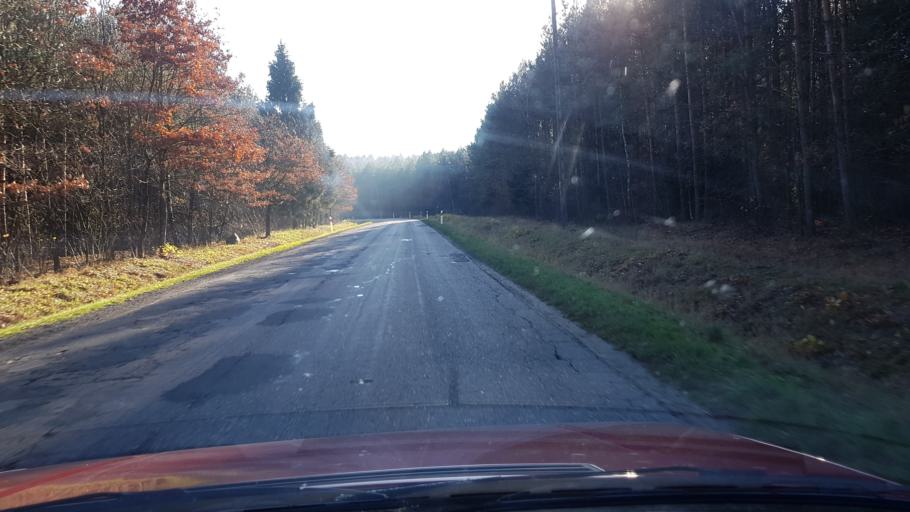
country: PL
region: West Pomeranian Voivodeship
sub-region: Powiat bialogardzki
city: Tychowo
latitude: 53.9795
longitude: 16.1884
